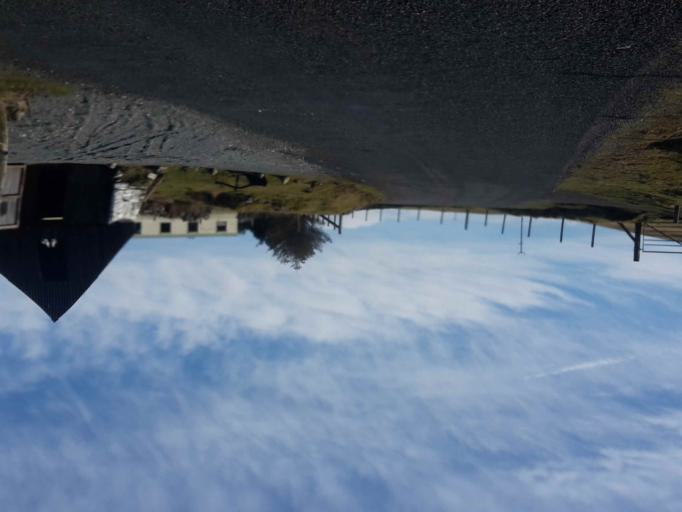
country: GB
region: Scotland
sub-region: Eilean Siar
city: Harris
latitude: 57.4465
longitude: -6.7217
